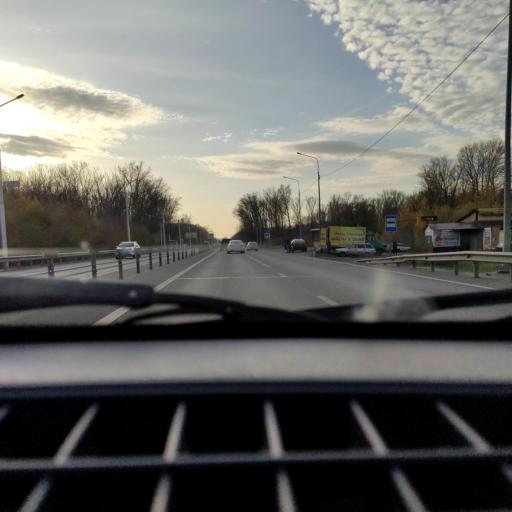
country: RU
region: Bashkortostan
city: Ufa
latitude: 54.7013
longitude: 55.9404
